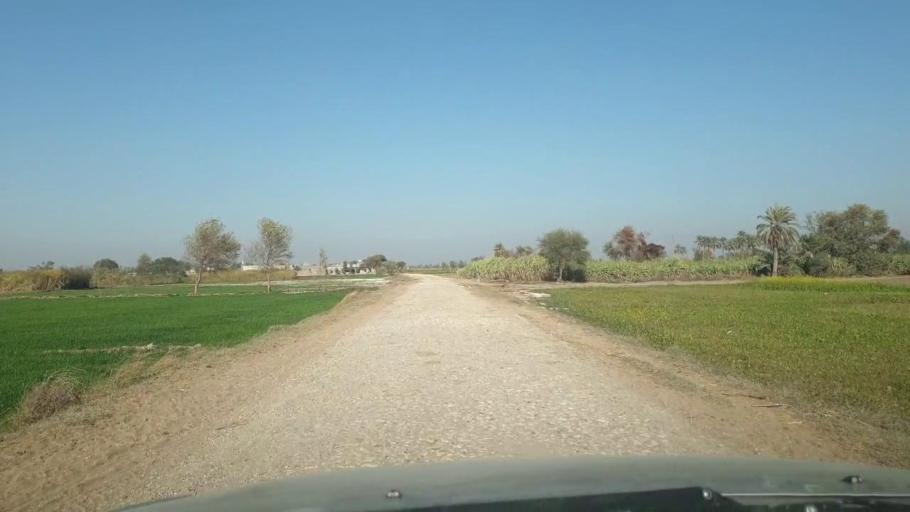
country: PK
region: Sindh
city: Ghotki
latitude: 28.0432
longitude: 69.3349
